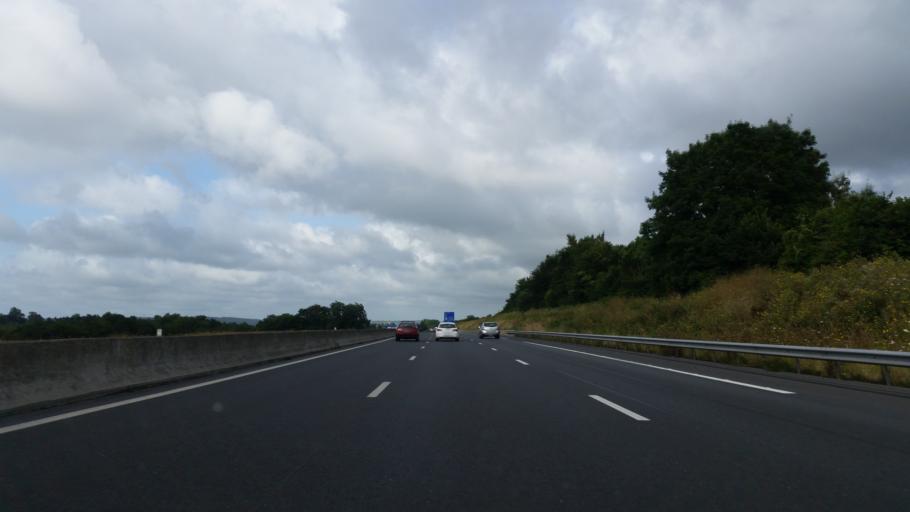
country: FR
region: Lower Normandy
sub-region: Departement du Calvados
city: Saint-Gatien-des-Bois
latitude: 49.2986
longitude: 0.2230
